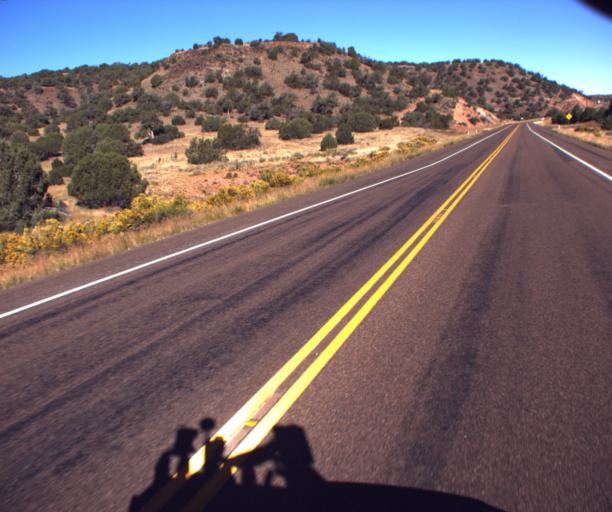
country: US
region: Arizona
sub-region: Navajo County
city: White Mountain Lake
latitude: 34.3864
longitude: -110.0616
